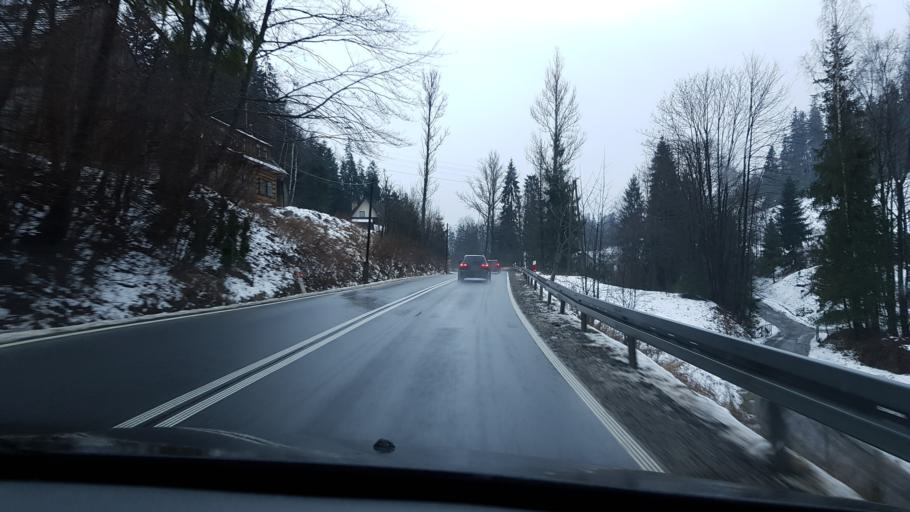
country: PL
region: Lesser Poland Voivodeship
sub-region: Powiat nowotarski
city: Sieniawa
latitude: 49.5192
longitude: 19.8920
